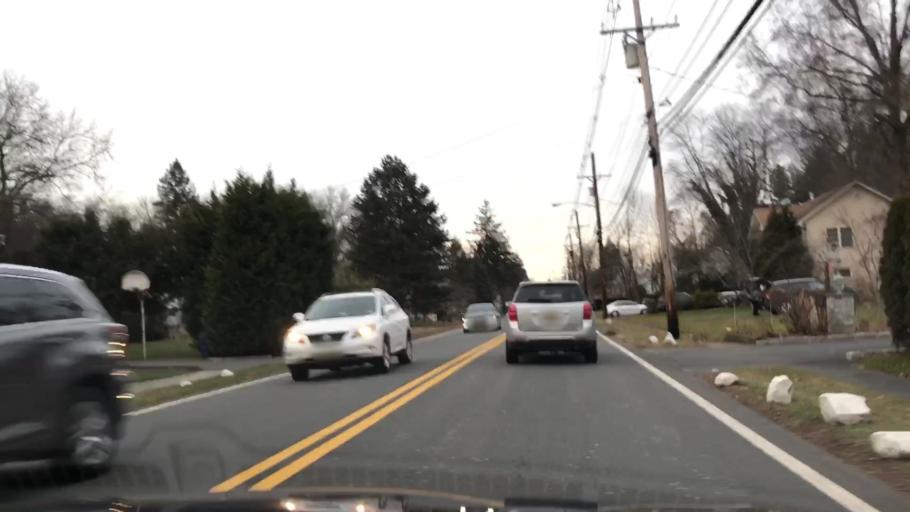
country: US
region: New Jersey
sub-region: Bergen County
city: Norwood
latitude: 40.9896
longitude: -73.9580
